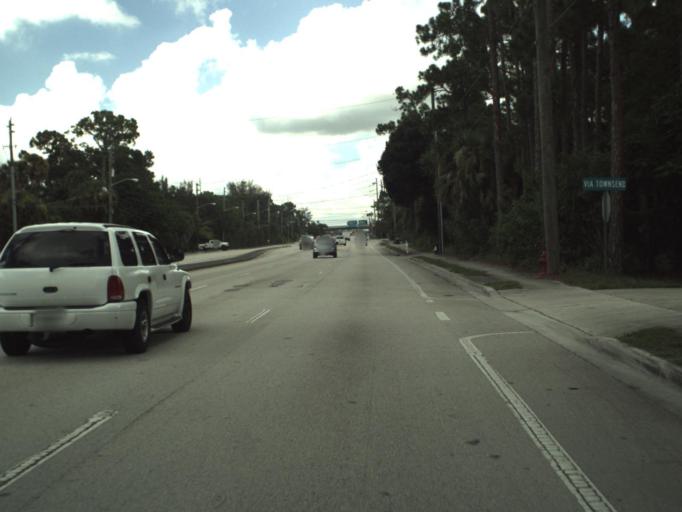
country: US
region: Florida
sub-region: Palm Beach County
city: Lake Belvedere Estates
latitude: 26.6717
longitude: -80.1450
